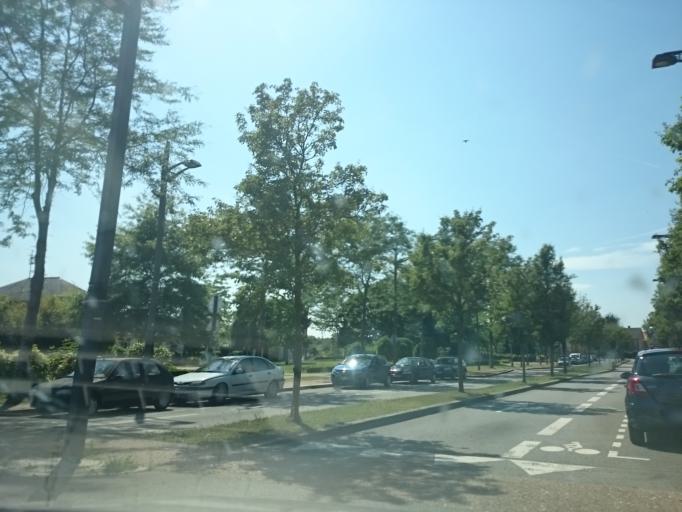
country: FR
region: Pays de la Loire
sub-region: Departement de la Loire-Atlantique
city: Coueron
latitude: 47.2092
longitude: -1.7281
